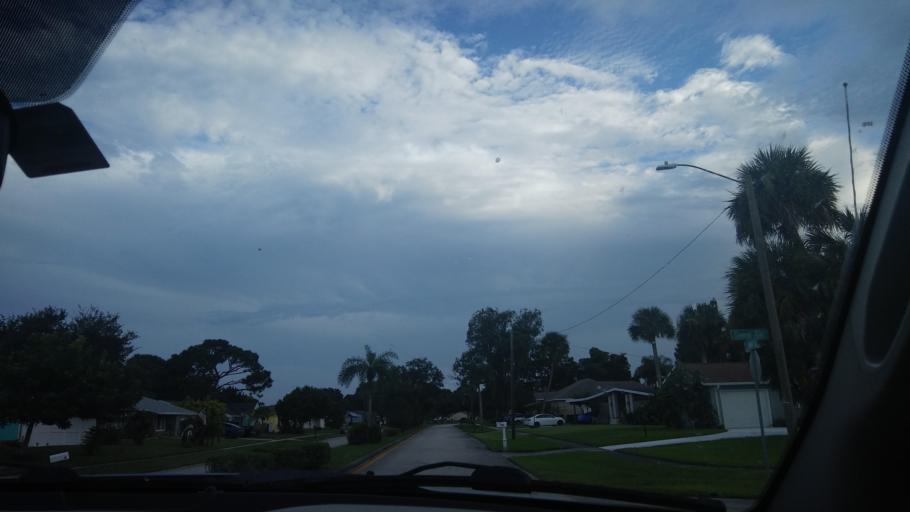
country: US
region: Florida
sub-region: Indian River County
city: Sebastian
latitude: 27.7836
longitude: -80.4628
